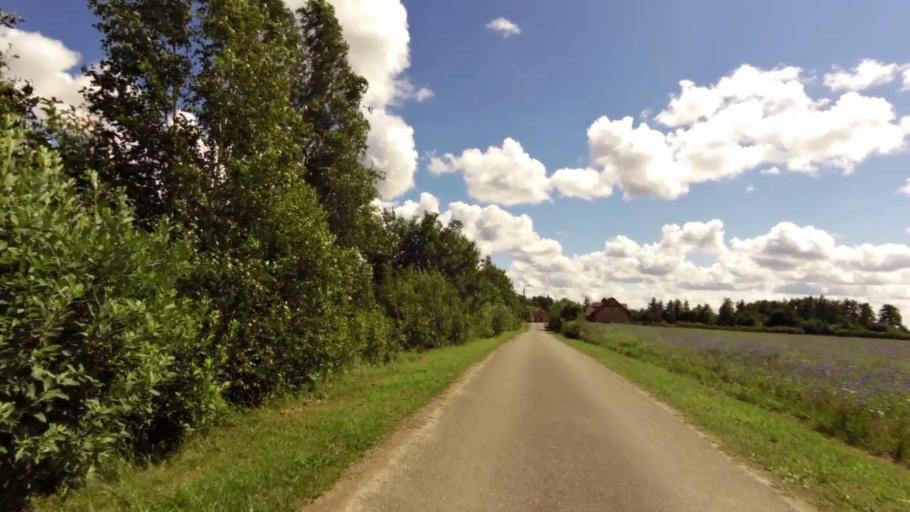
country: PL
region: West Pomeranian Voivodeship
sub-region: Powiat slawienski
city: Slawno
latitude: 54.5259
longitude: 16.6075
